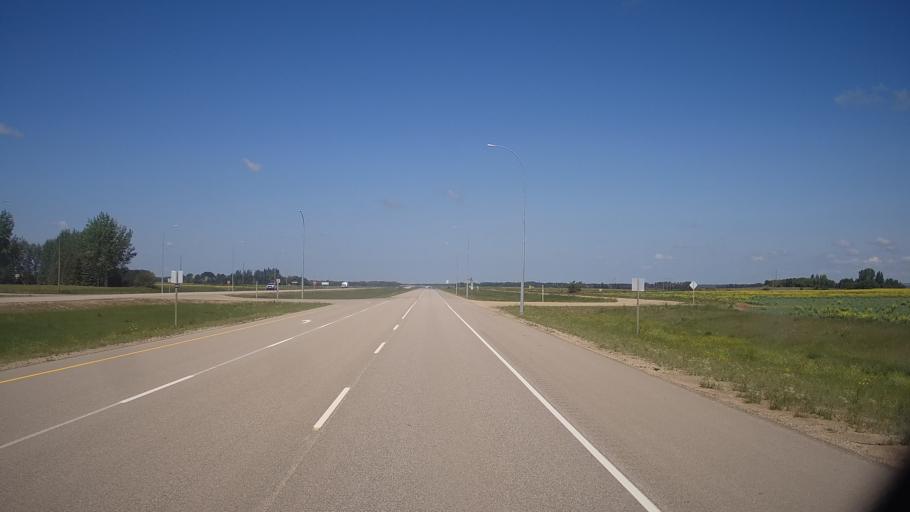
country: CA
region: Saskatchewan
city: Saskatoon
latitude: 52.0006
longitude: -106.3309
